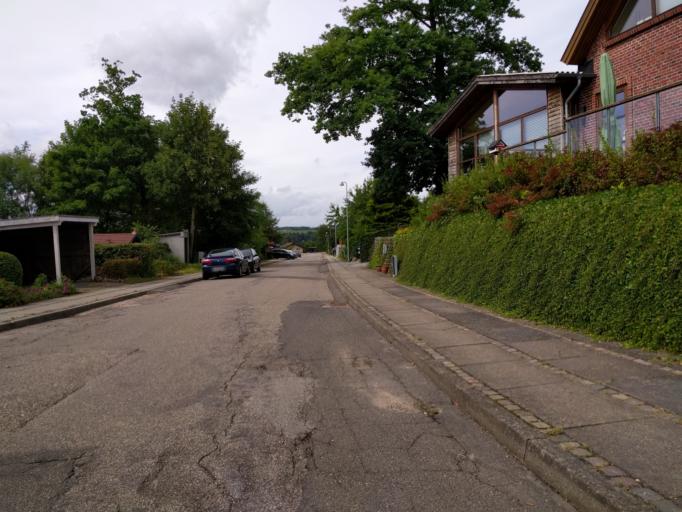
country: DK
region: Central Jutland
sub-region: Skanderborg Kommune
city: Ry
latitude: 56.0940
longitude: 9.7659
